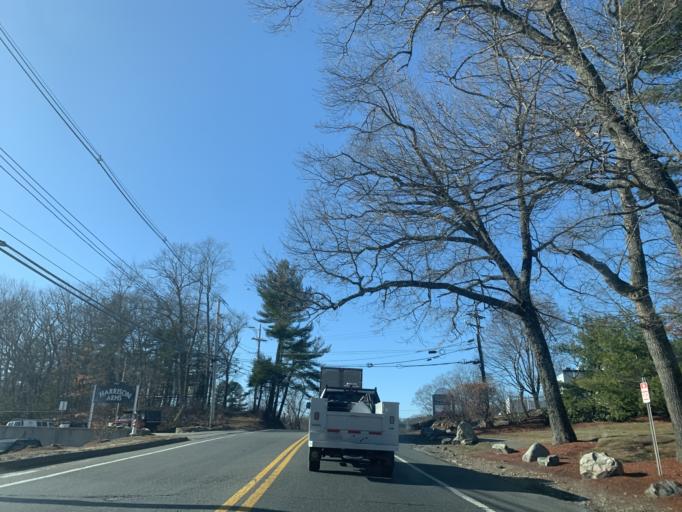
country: US
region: Massachusetts
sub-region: Middlesex County
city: Marlborough
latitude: 42.3476
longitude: -71.5125
